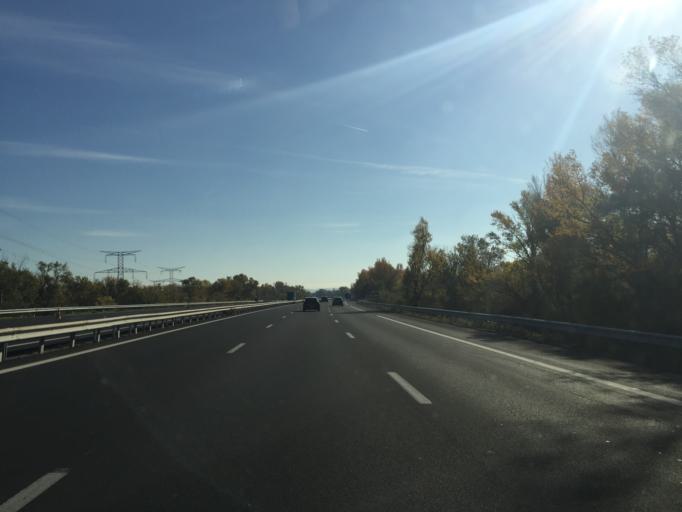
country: FR
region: Provence-Alpes-Cote d'Azur
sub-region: Departement des Bouches-du-Rhone
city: Cabannes
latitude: 43.8492
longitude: 4.9885
